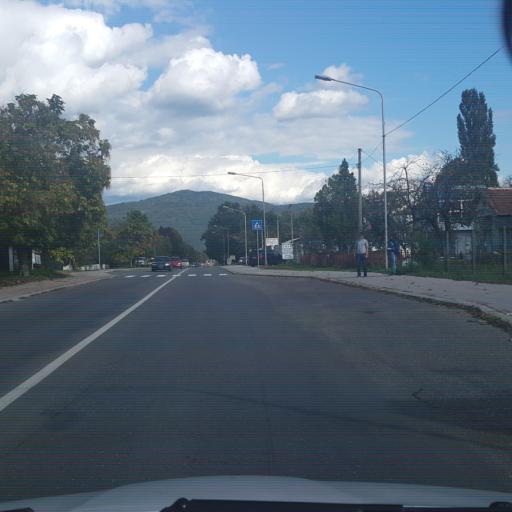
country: RS
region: Central Serbia
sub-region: Raski Okrug
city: Vrnjacka Banja
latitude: 43.6345
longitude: 20.9092
